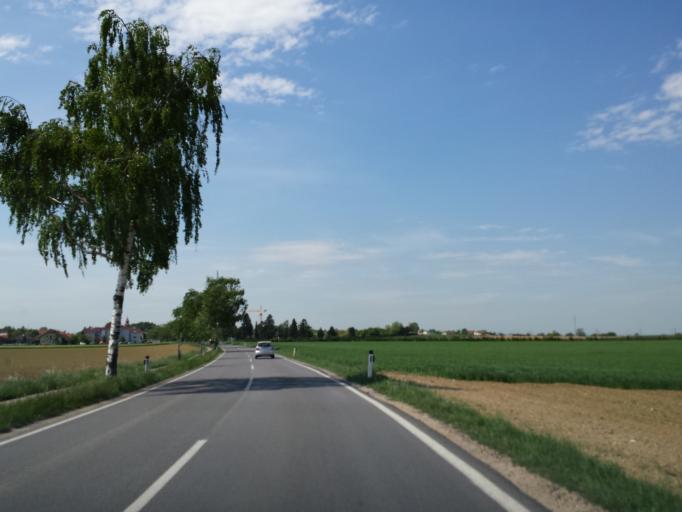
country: AT
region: Lower Austria
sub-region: Politischer Bezirk Tulln
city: Atzenbrugg
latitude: 48.2945
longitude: 15.9026
